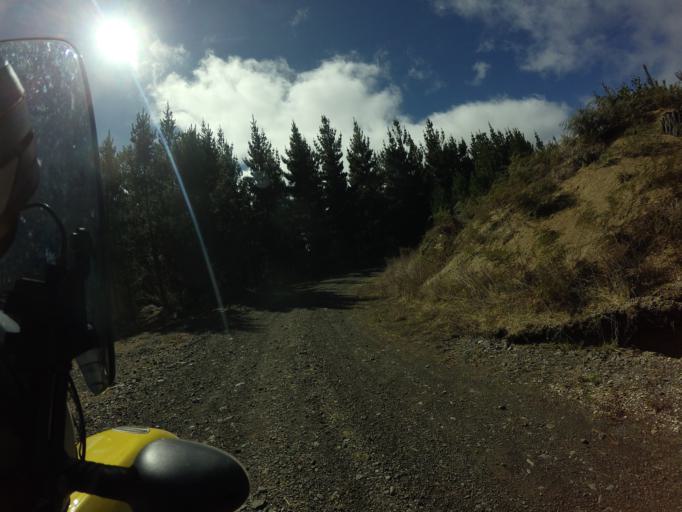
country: NZ
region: Bay of Plenty
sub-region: Whakatane District
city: Murupara
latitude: -38.8201
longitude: 176.5509
